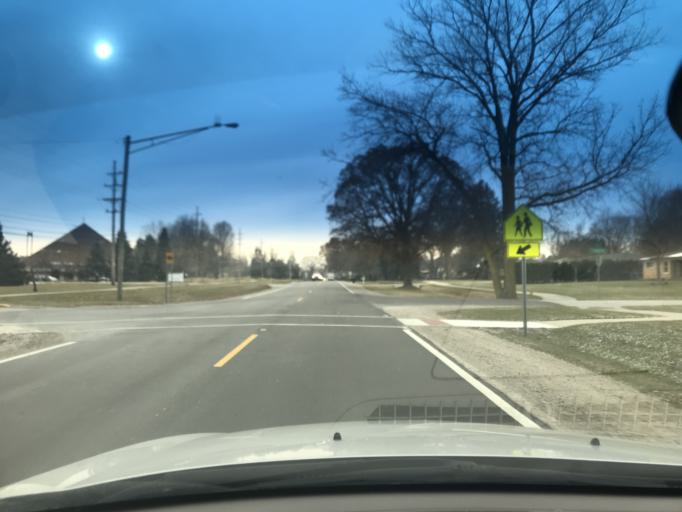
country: US
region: Michigan
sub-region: Macomb County
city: Shelby
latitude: 42.6897
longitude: -83.0543
